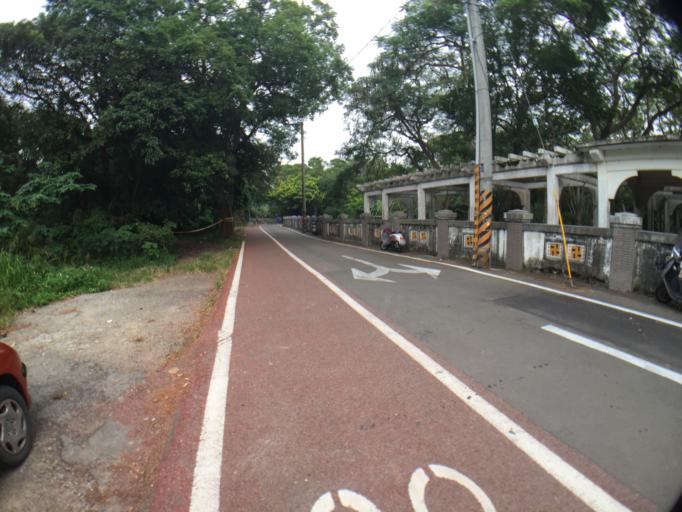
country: TW
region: Taiwan
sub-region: Hsinchu
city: Hsinchu
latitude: 24.7730
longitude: 120.9714
